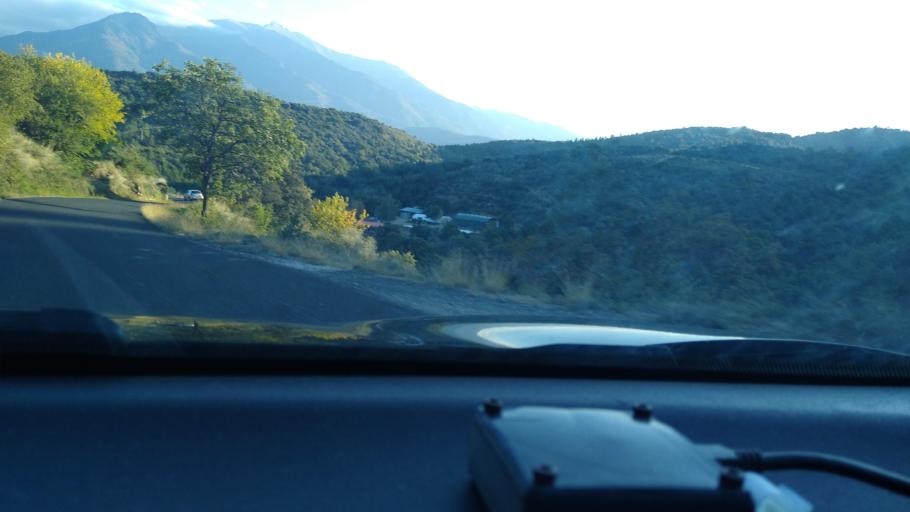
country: FR
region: Languedoc-Roussillon
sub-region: Departement des Pyrenees-Orientales
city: Ria-Sirach
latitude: 42.6363
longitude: 2.4157
